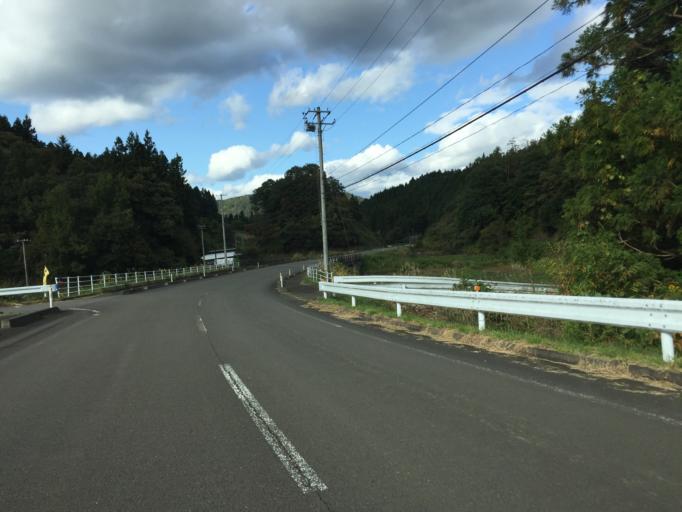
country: JP
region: Miyagi
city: Marumori
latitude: 37.8194
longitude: 140.7296
